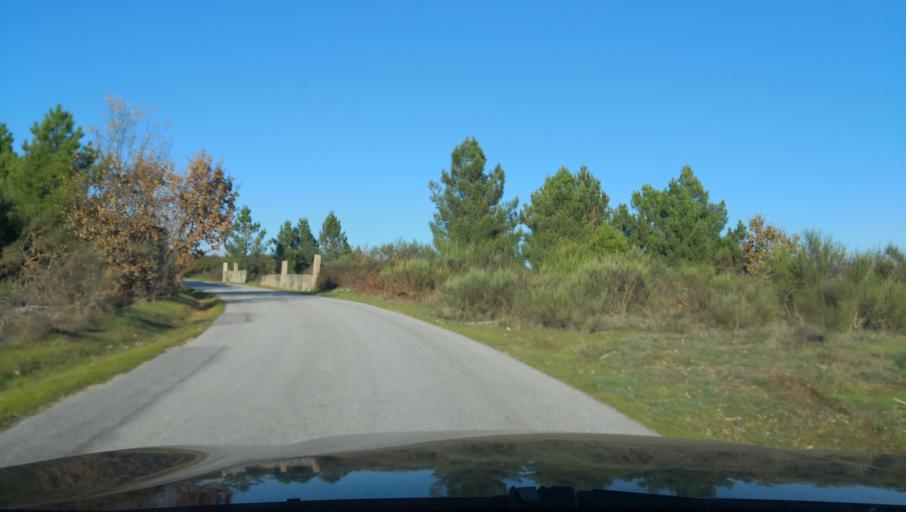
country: PT
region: Vila Real
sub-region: Vila Real
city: Vila Real
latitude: 41.3460
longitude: -7.6634
